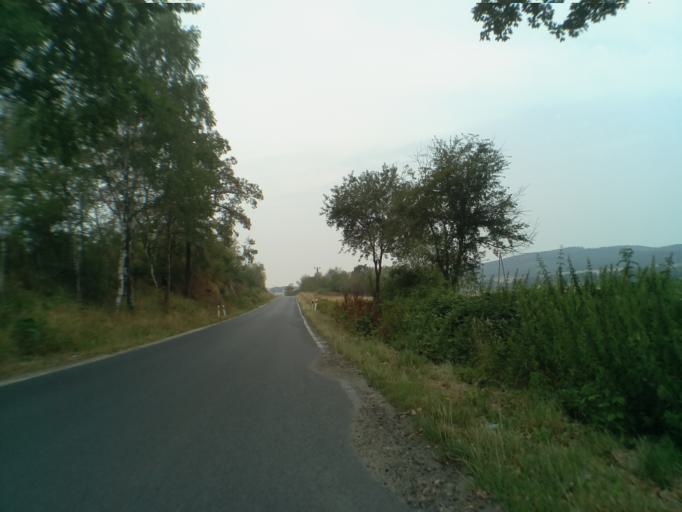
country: PL
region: Lower Silesian Voivodeship
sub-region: Powiat swidnicki
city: Strzegom
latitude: 50.9694
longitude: 16.3226
